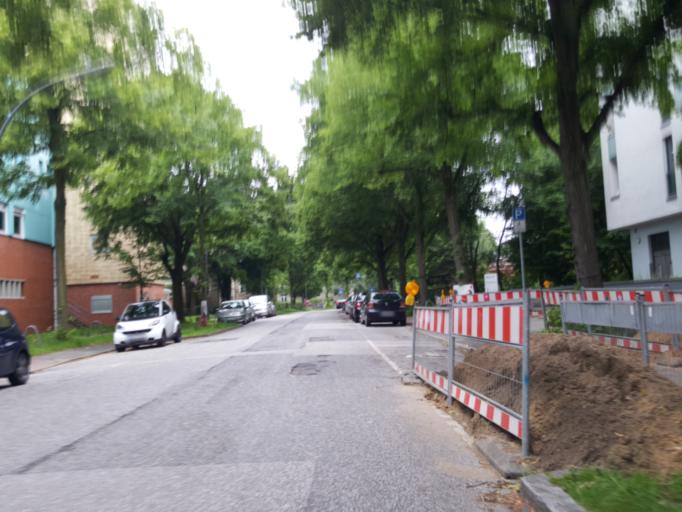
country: DE
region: Hamburg
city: Marienthal
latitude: 53.5553
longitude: 10.0721
